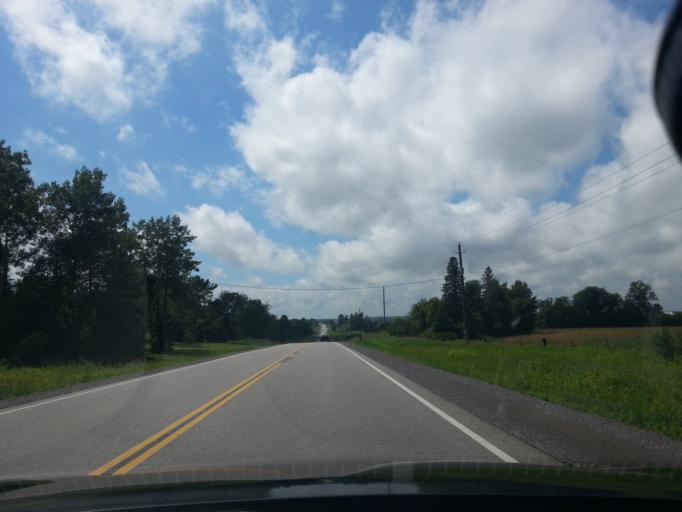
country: CA
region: Ontario
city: Renfrew
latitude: 45.5200
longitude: -76.8502
